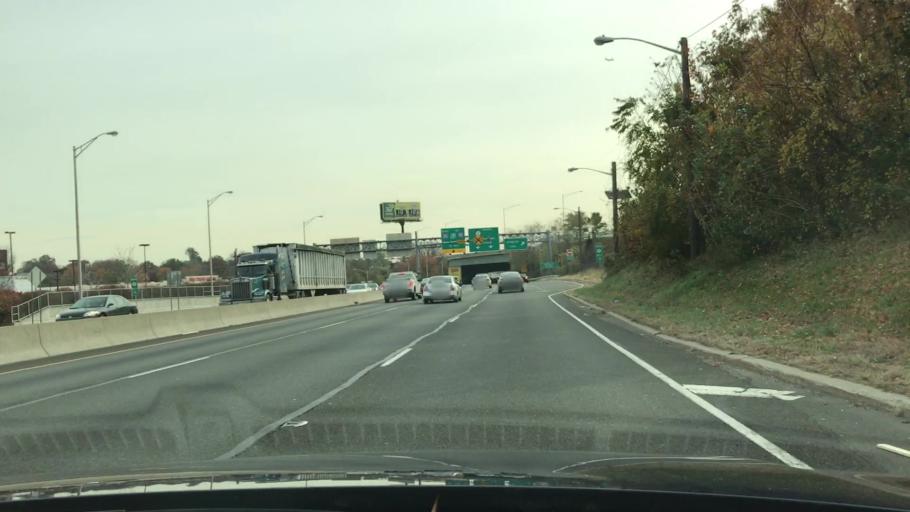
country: US
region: New Jersey
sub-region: Bergen County
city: Lodi
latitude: 40.8886
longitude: -74.0695
